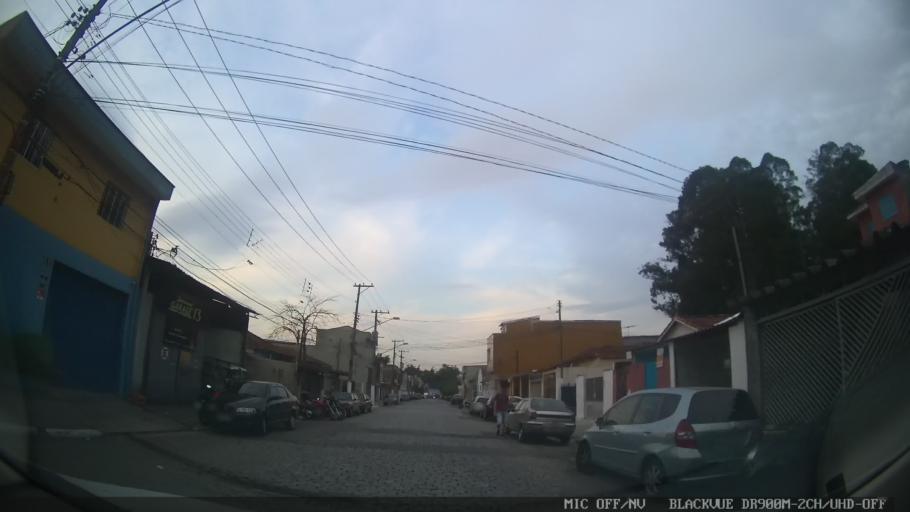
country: BR
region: Sao Paulo
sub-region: Sao Caetano Do Sul
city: Sao Caetano do Sul
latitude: -23.6042
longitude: -46.5879
